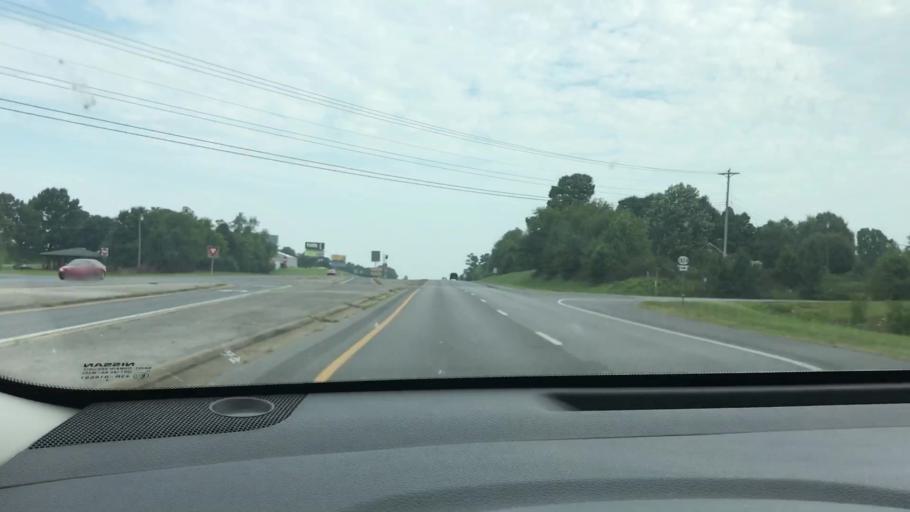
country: US
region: Kentucky
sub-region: Calloway County
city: Murray
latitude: 36.6760
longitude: -88.3025
